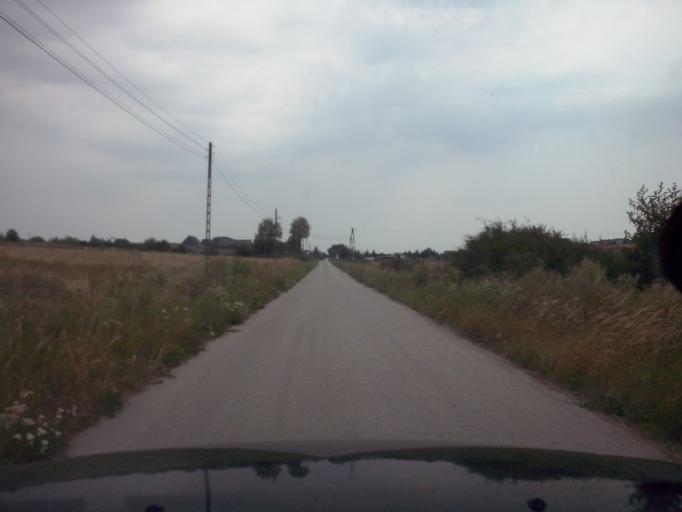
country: PL
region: Swietokrzyskie
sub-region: Powiat kielecki
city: Brzeziny
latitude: 50.7830
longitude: 20.5475
